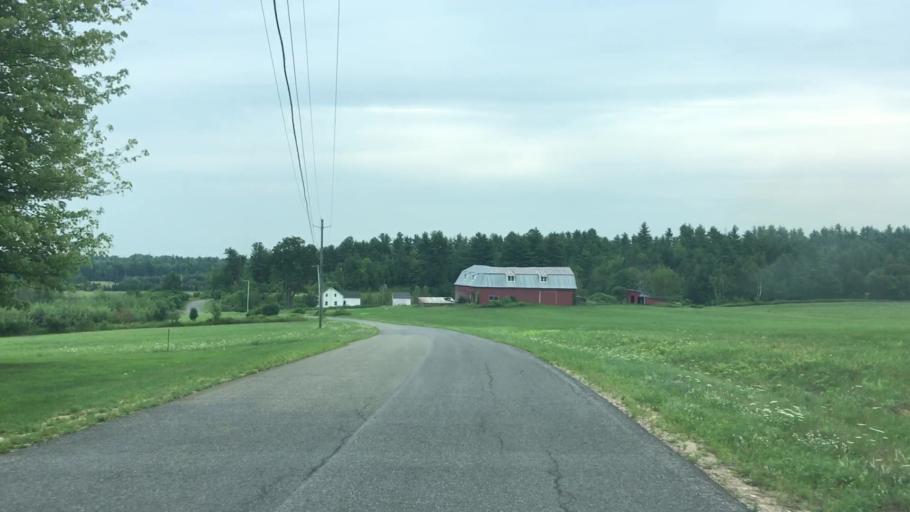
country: US
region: New York
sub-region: Clinton County
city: Peru
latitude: 44.6041
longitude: -73.6182
